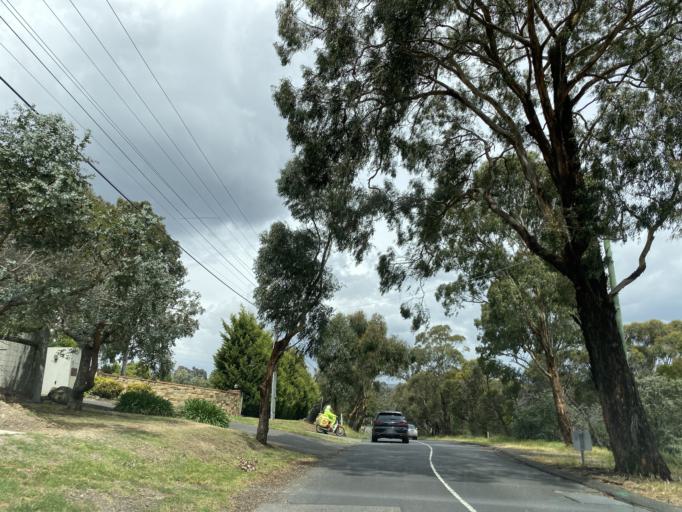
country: AU
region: Victoria
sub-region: Banyule
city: Lower Plenty
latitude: -37.7341
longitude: 145.1193
